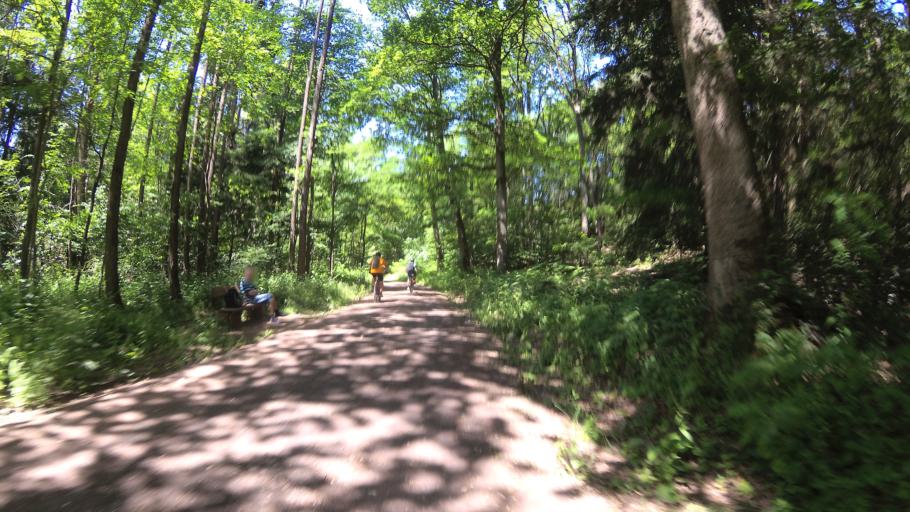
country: DE
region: Saarland
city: Saarwellingen
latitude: 49.3674
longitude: 6.8010
